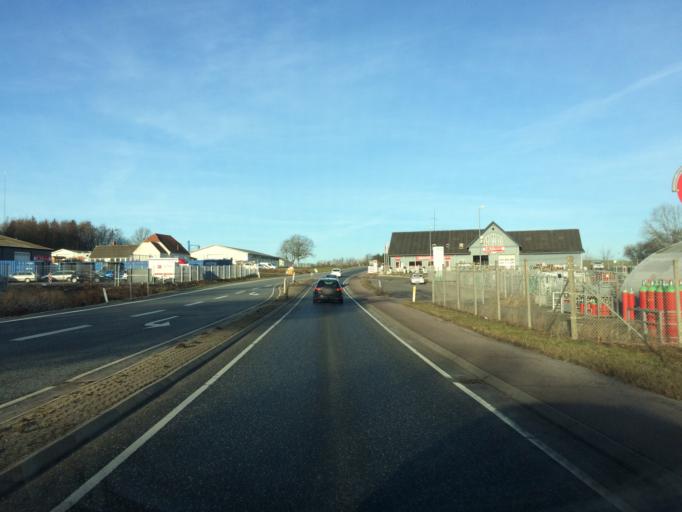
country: DK
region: South Denmark
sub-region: Fredericia Kommune
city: Snoghoj
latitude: 55.5435
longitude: 9.6829
